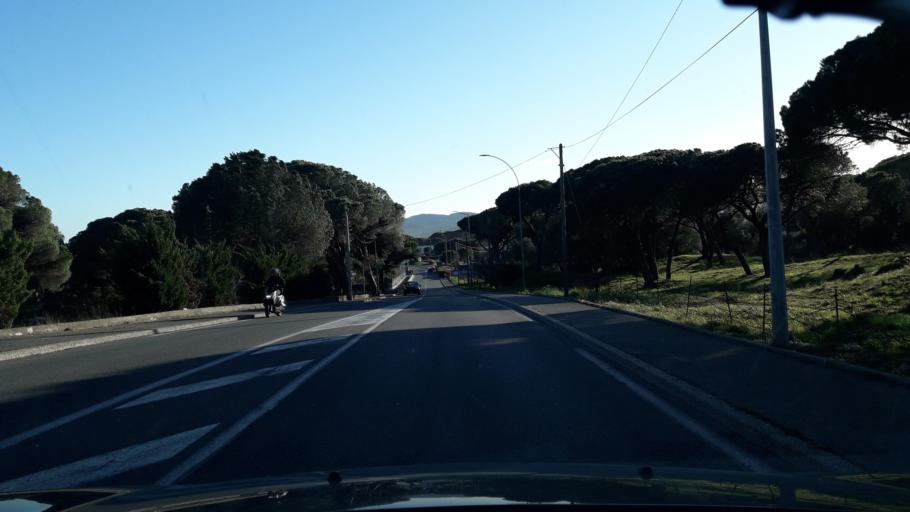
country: FR
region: Provence-Alpes-Cote d'Azur
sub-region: Departement du Var
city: Frejus
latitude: 43.4562
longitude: 6.7279
